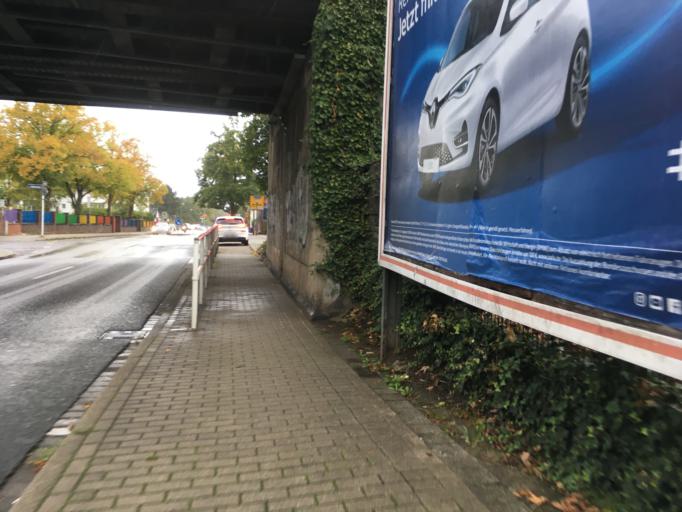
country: DE
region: North Rhine-Westphalia
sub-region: Regierungsbezirk Munster
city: Bottrop
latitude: 51.4859
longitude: 6.9327
